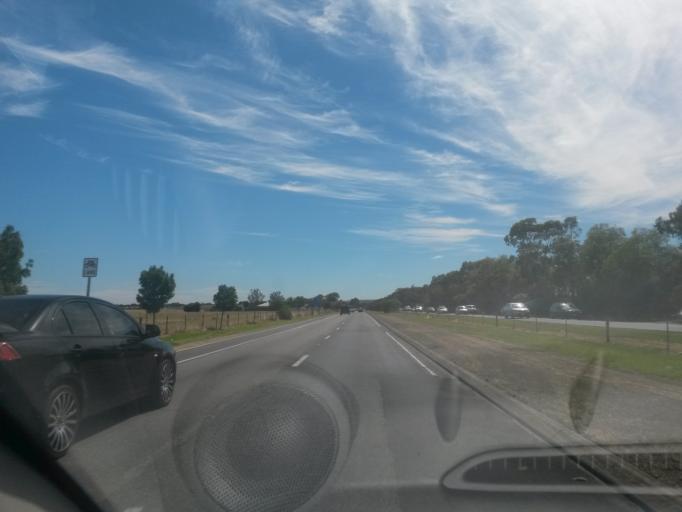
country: AU
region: South Australia
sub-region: Salisbury
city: Salisbury
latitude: -34.7998
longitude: 138.6396
